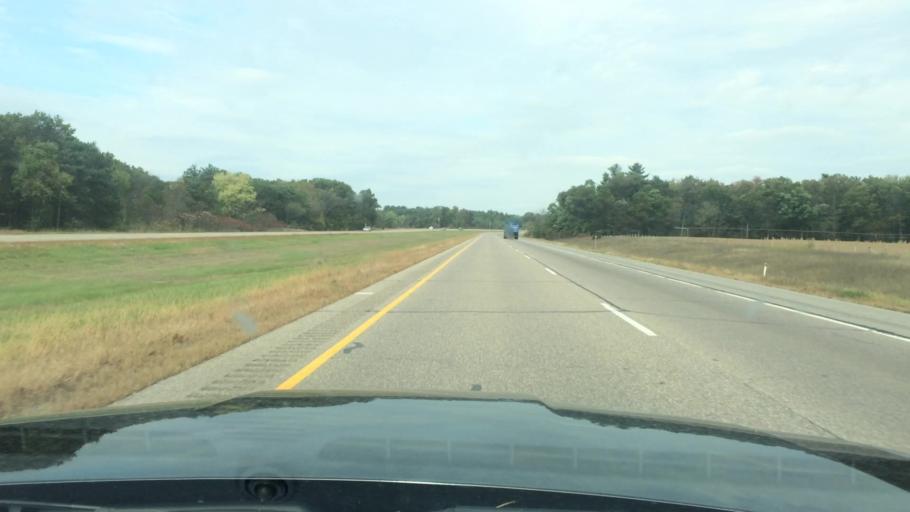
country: US
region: Wisconsin
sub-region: Portage County
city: Stevens Point
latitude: 44.6563
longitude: -89.6409
